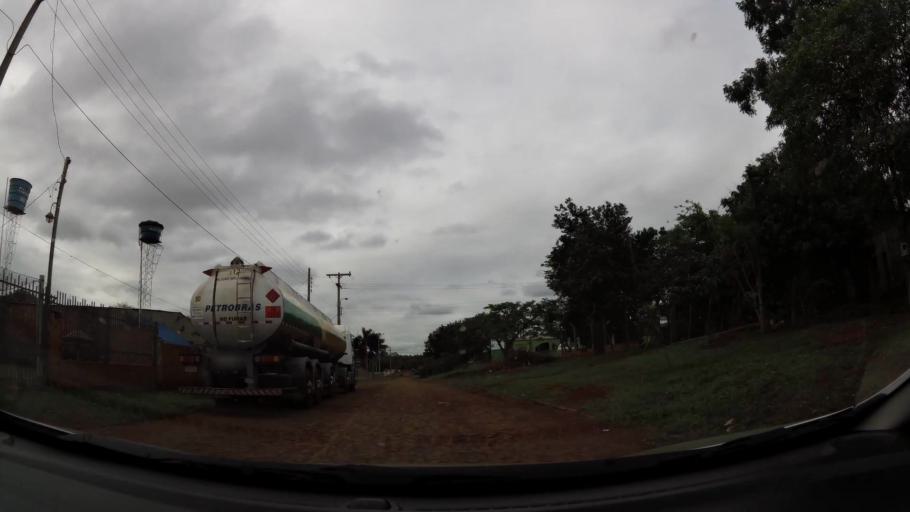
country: PY
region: Alto Parana
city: Ciudad del Este
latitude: -25.4033
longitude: -54.6357
